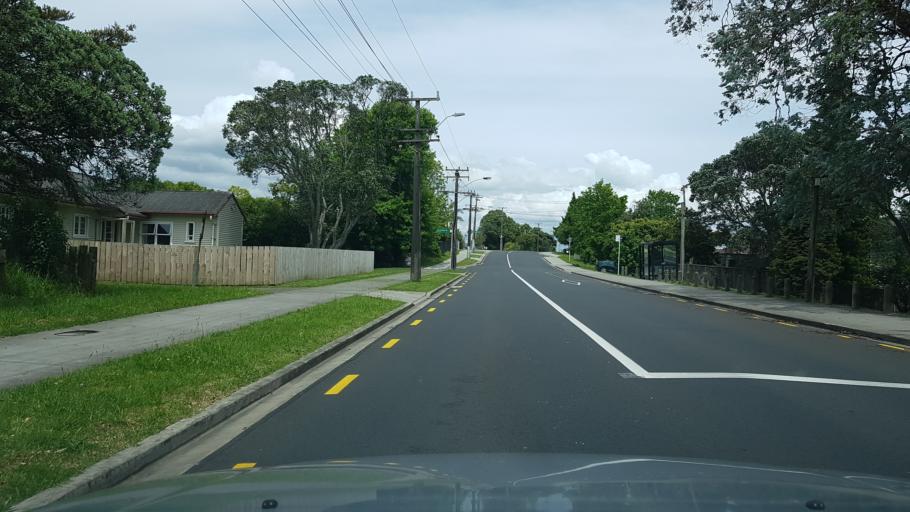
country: NZ
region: Auckland
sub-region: Auckland
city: North Shore
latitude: -36.7978
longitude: 174.7522
